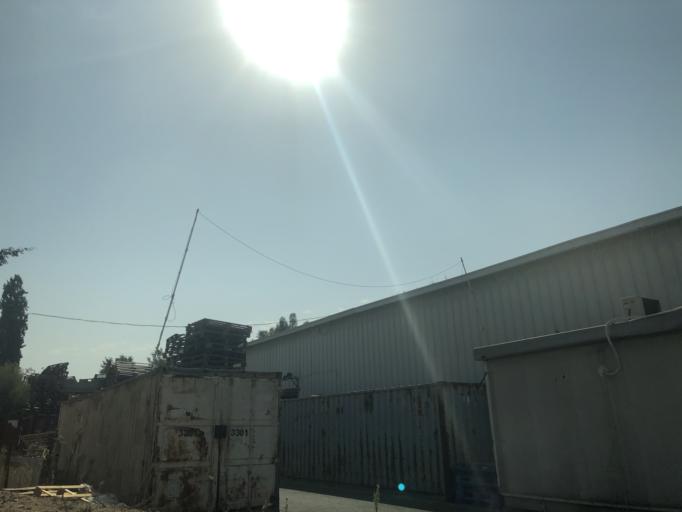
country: IL
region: Central District
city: Nehalim
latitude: 32.0584
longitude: 34.9487
